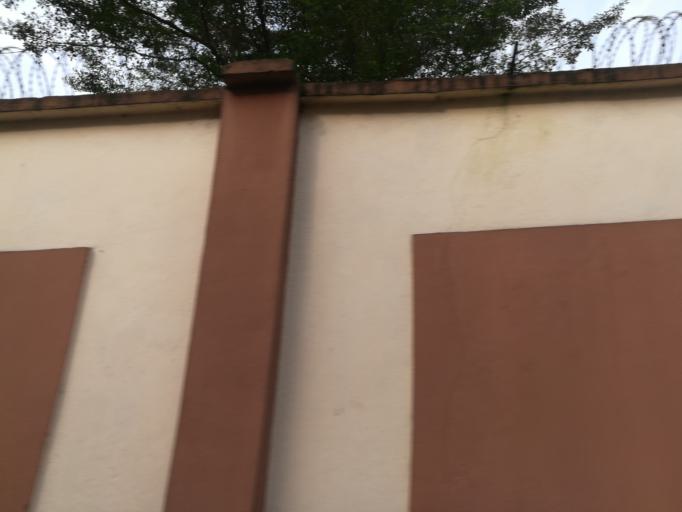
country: NG
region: Rivers
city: Port Harcourt
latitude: 4.8433
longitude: 7.0535
